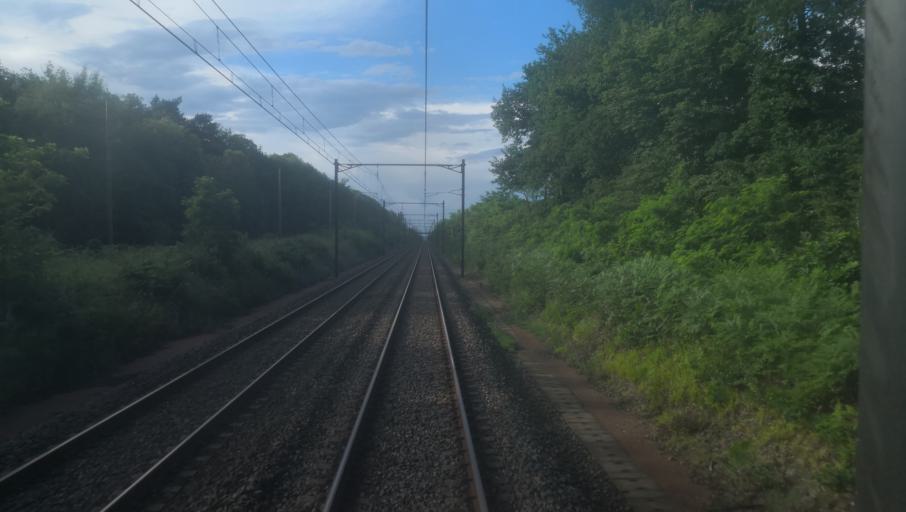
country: FR
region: Centre
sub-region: Departement du Loir-et-Cher
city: Nouan-le-Fuzelier
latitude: 47.4968
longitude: 2.0371
